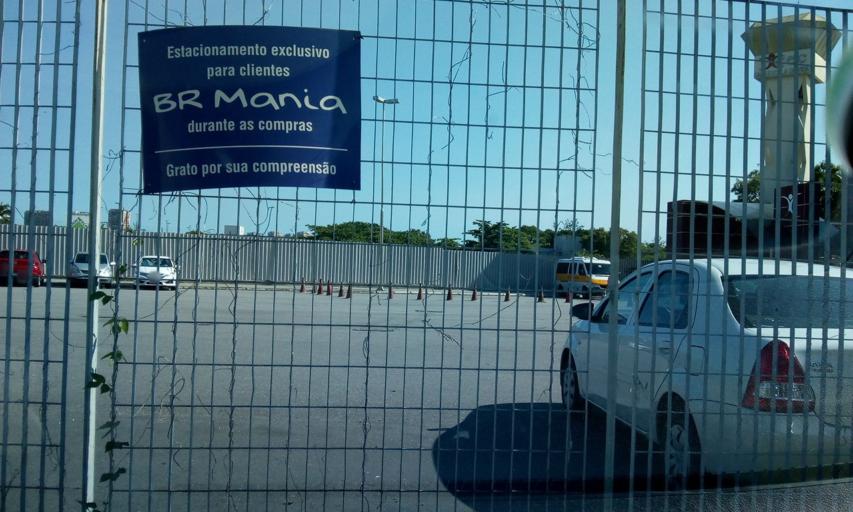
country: BR
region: Rio de Janeiro
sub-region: Rio De Janeiro
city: Rio de Janeiro
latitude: -22.9899
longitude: -43.3668
